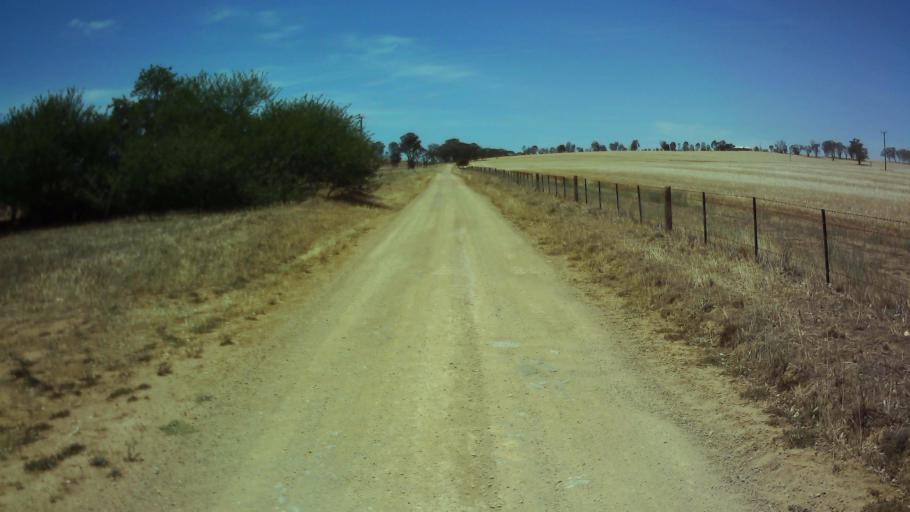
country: AU
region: New South Wales
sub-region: Weddin
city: Grenfell
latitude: -33.9298
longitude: 148.1638
